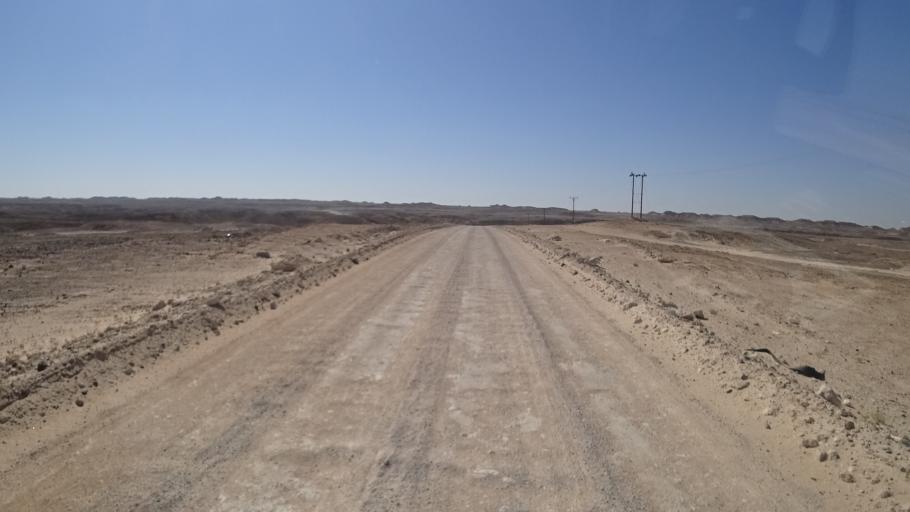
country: YE
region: Al Mahrah
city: Hawf
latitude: 17.3748
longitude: 53.2006
